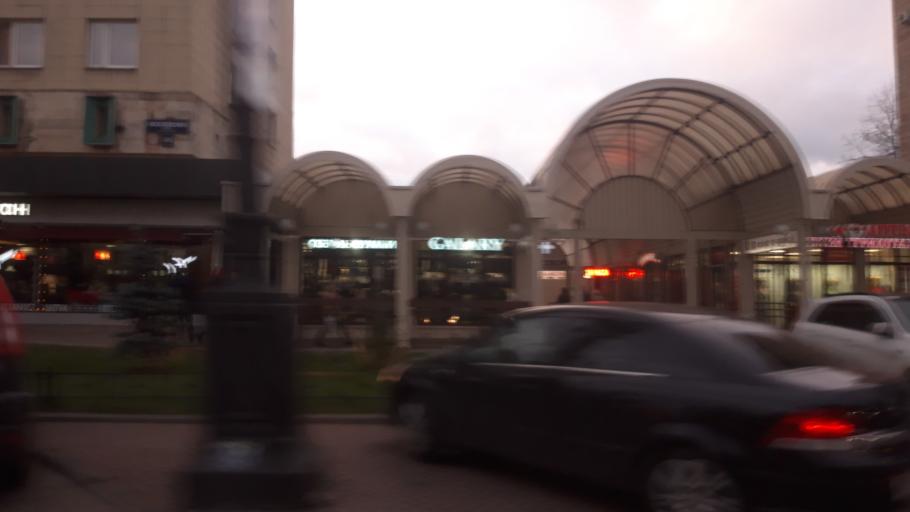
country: RU
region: St.-Petersburg
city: Kupchino
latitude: 59.8482
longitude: 30.3211
